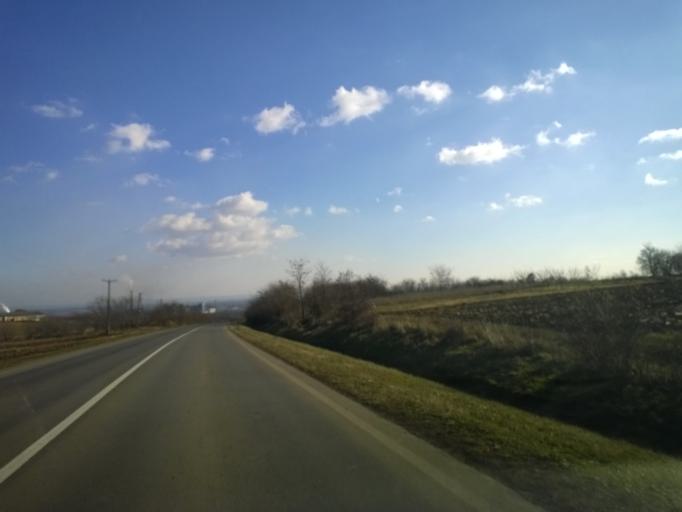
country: RS
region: Central Serbia
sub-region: Podunavski Okrug
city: Smederevo
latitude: 44.6113
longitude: 20.9324
